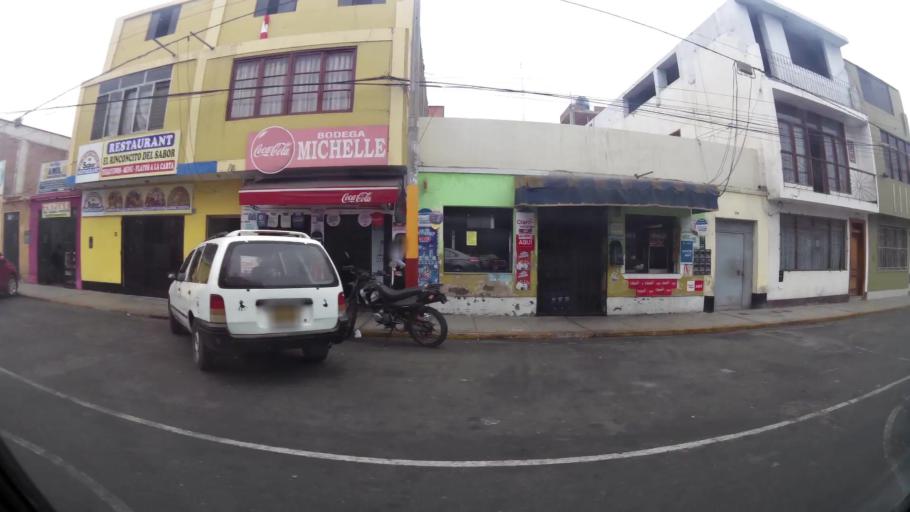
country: PE
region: Ancash
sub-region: Provincia de Santa
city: Chimbote
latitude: -9.0737
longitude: -78.5946
